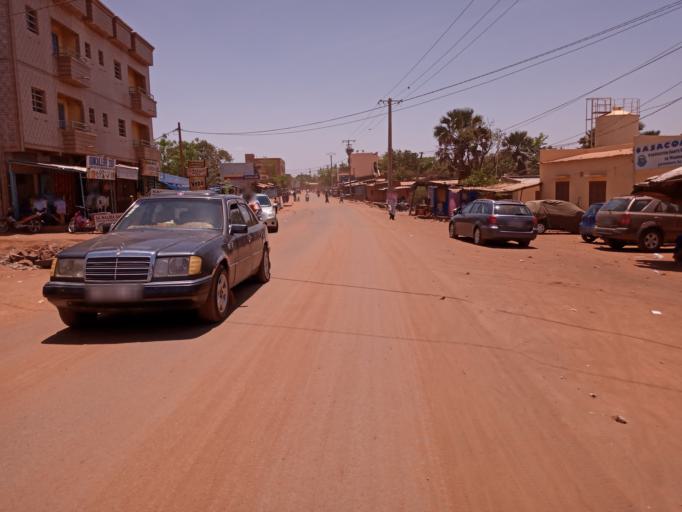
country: ML
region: Bamako
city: Bamako
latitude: 12.5805
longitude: -7.9720
